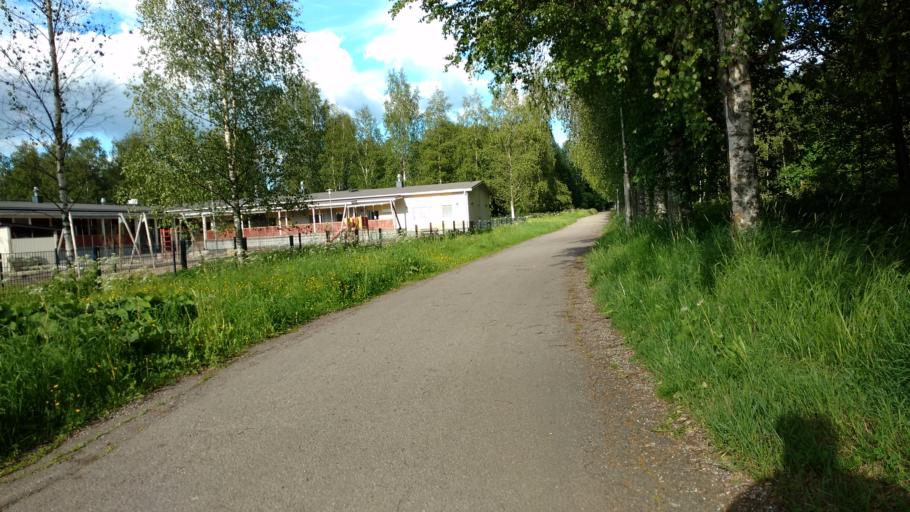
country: FI
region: Varsinais-Suomi
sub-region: Salo
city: Salo
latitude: 60.3860
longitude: 23.1505
